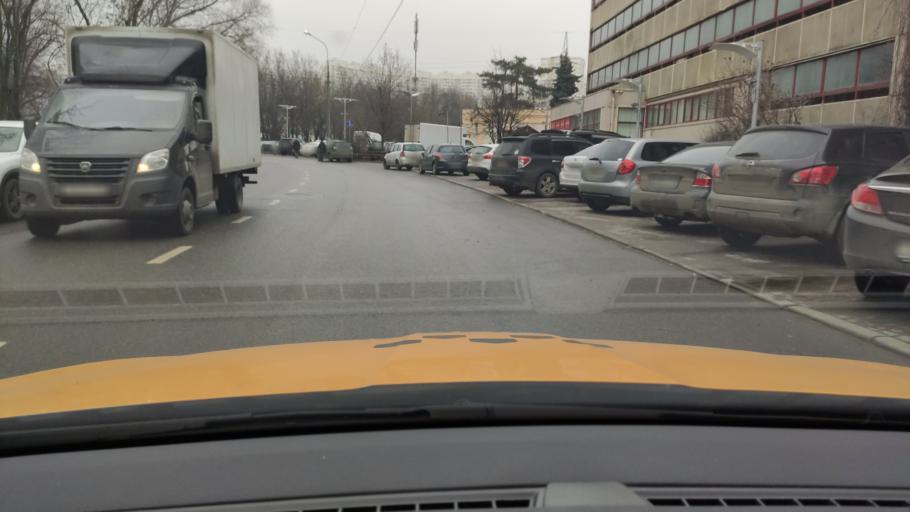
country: RU
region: Moscow
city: Khimki
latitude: 55.8811
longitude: 37.4317
